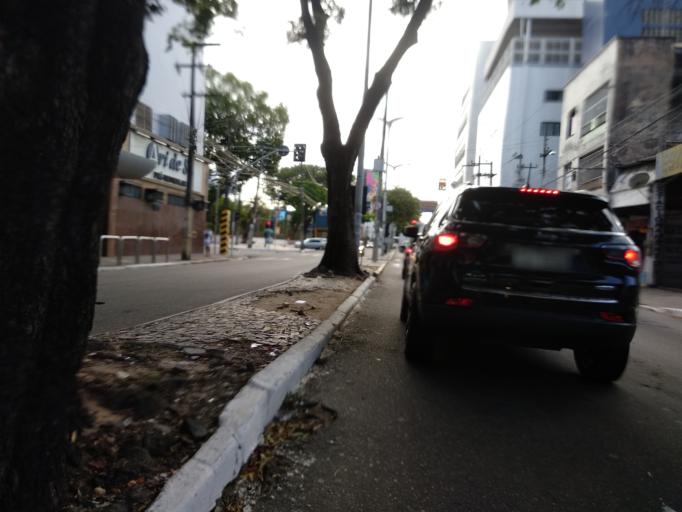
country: BR
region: Ceara
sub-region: Fortaleza
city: Fortaleza
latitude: -3.7323
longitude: -38.5284
